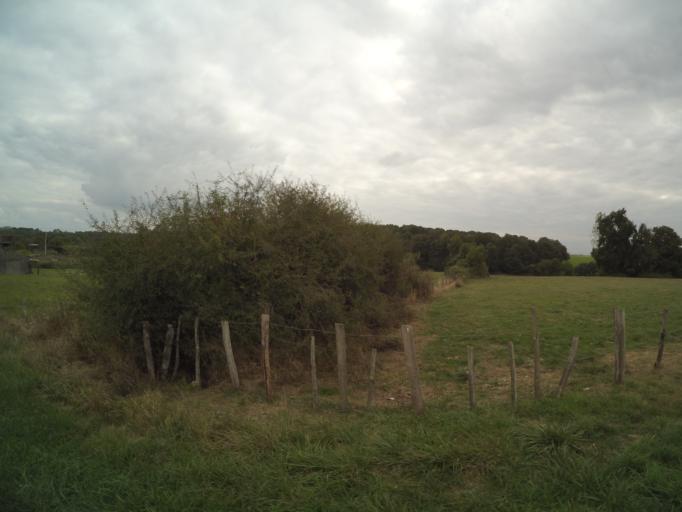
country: FR
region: Centre
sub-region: Departement d'Indre-et-Loire
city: Auzouer-en-Touraine
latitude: 47.5089
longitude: 0.9417
